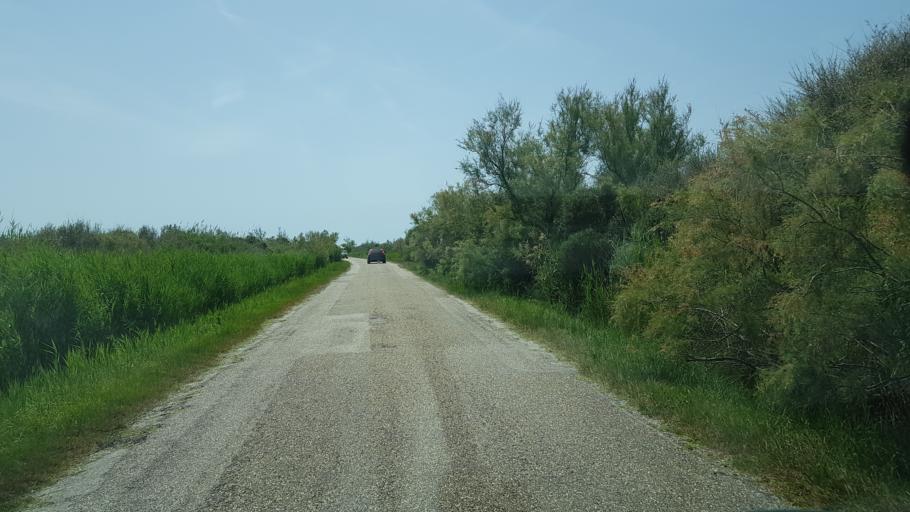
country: FR
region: Provence-Alpes-Cote d'Azur
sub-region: Departement des Bouches-du-Rhone
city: Arles
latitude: 43.4784
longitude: 4.6480
